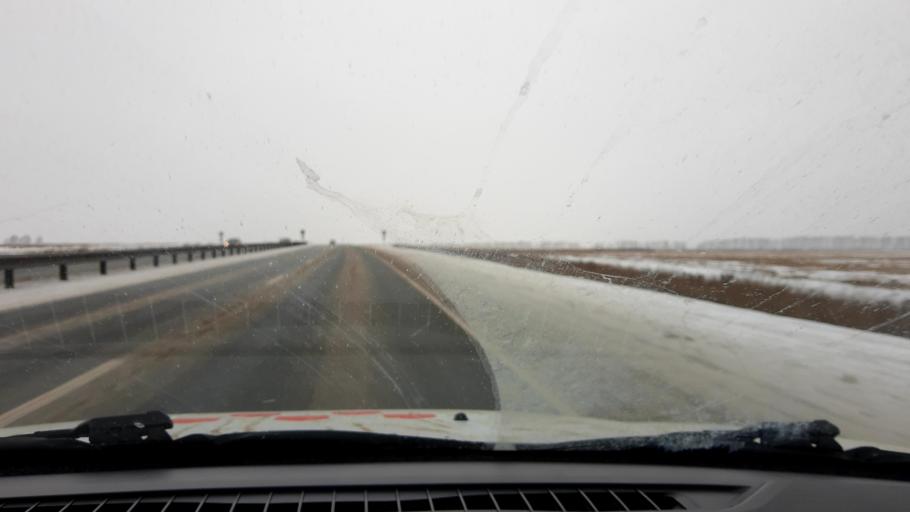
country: RU
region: Nizjnij Novgorod
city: Burevestnik
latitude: 56.1175
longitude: 43.9527
